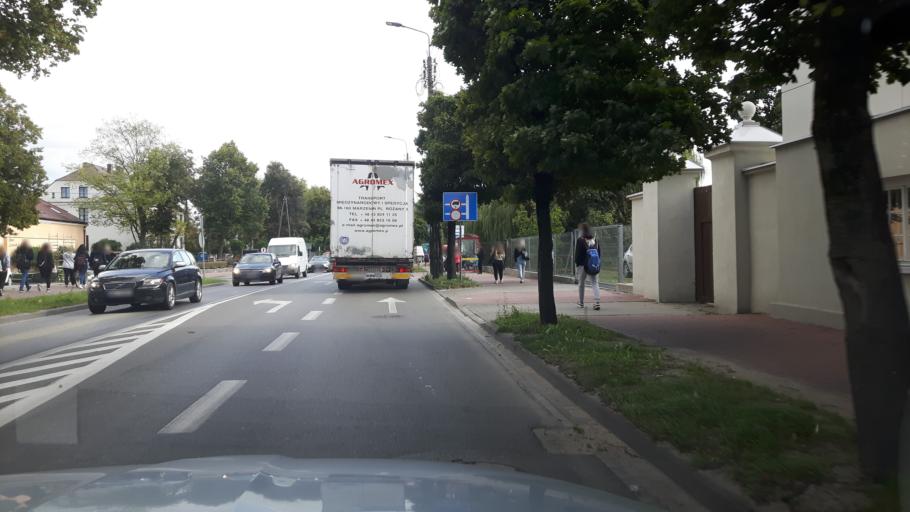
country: PL
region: Masovian Voivodeship
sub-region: Powiat wolominski
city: Radzymin
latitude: 52.4149
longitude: 21.1873
